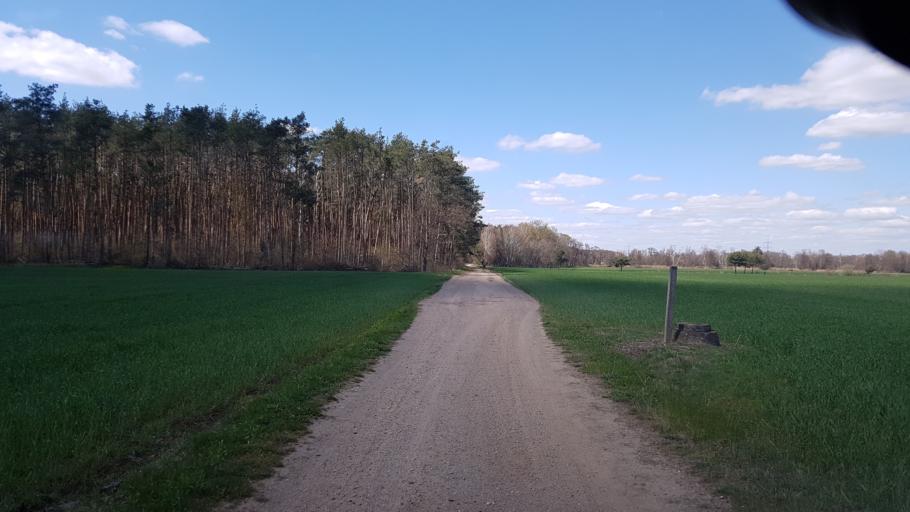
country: DE
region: Brandenburg
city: Bad Liebenwerda
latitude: 51.5198
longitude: 13.4381
